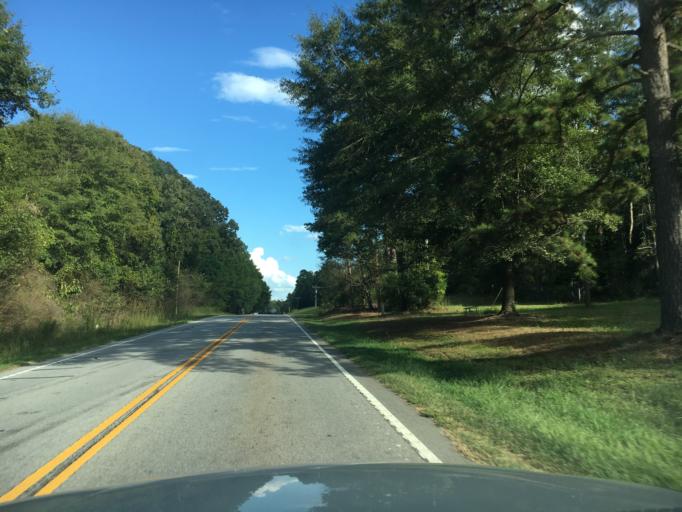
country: US
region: South Carolina
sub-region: Laurens County
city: Laurens
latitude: 34.5214
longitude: -82.1146
